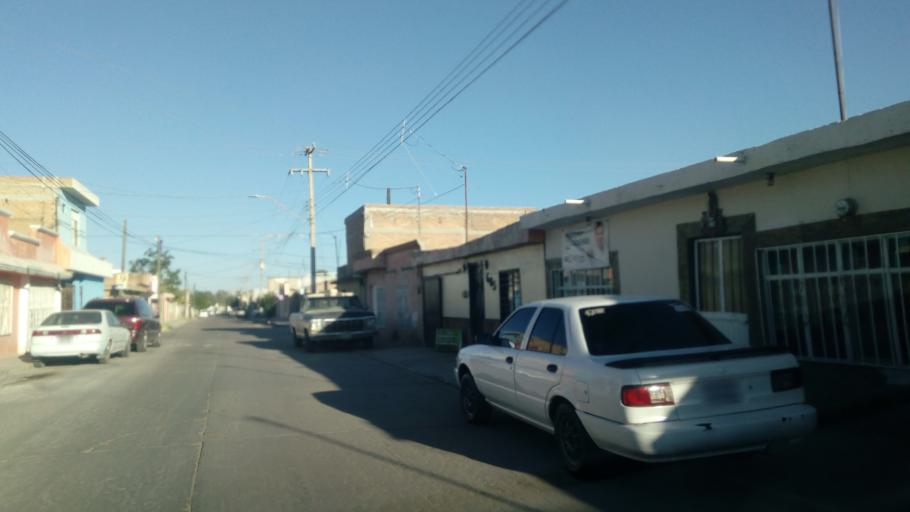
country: MX
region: Durango
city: Victoria de Durango
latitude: 23.9981
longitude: -104.6824
